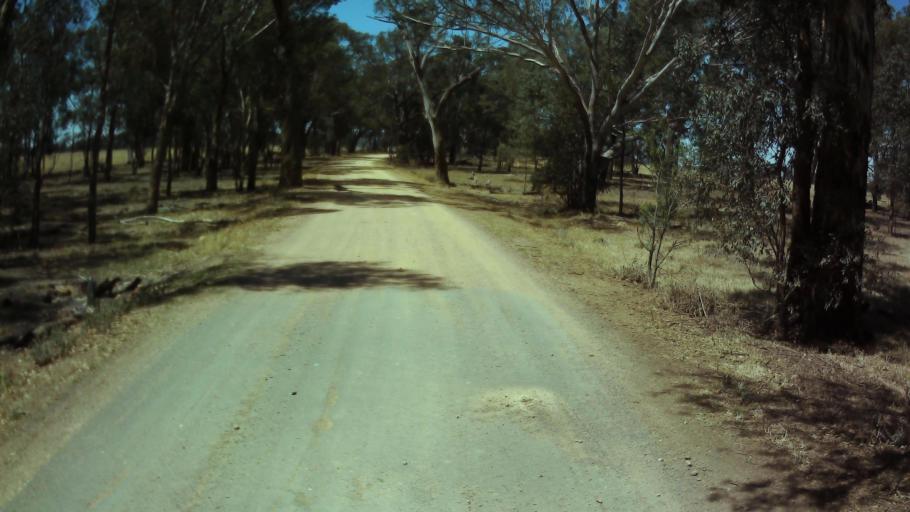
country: AU
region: New South Wales
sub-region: Weddin
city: Grenfell
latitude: -34.0328
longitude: 148.0137
